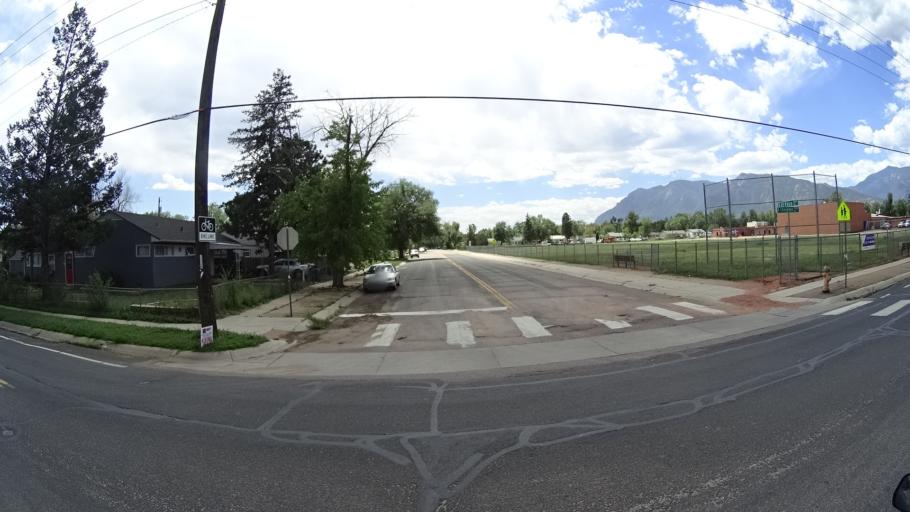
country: US
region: Colorado
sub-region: El Paso County
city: Colorado Springs
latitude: 38.8068
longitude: -104.8112
